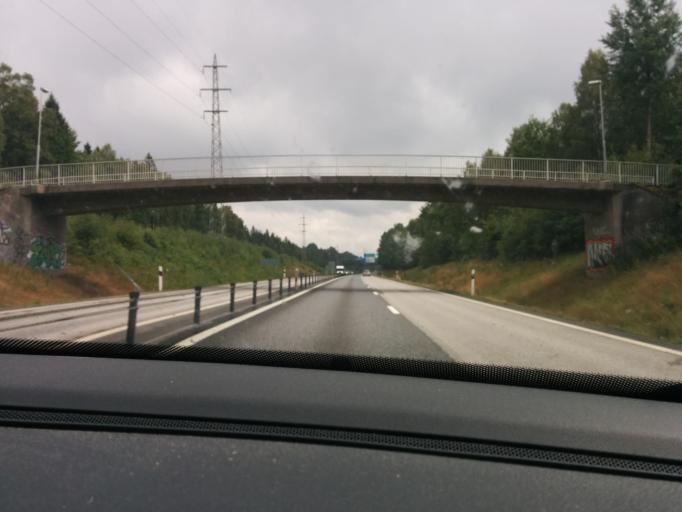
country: SE
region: Kronoberg
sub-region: Vaxjo Kommun
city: Vaexjoe
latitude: 56.9018
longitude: 14.8029
